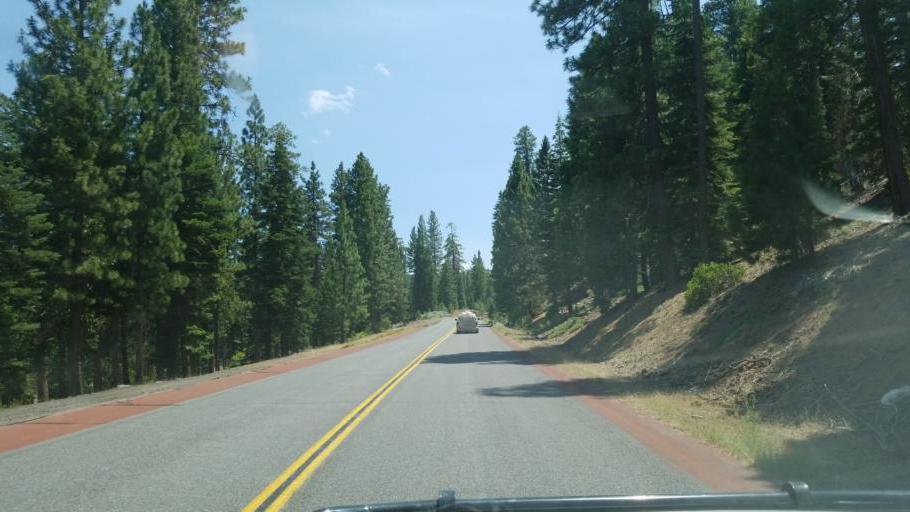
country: US
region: California
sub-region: Lassen County
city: Susanville
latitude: 40.5597
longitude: -120.8277
